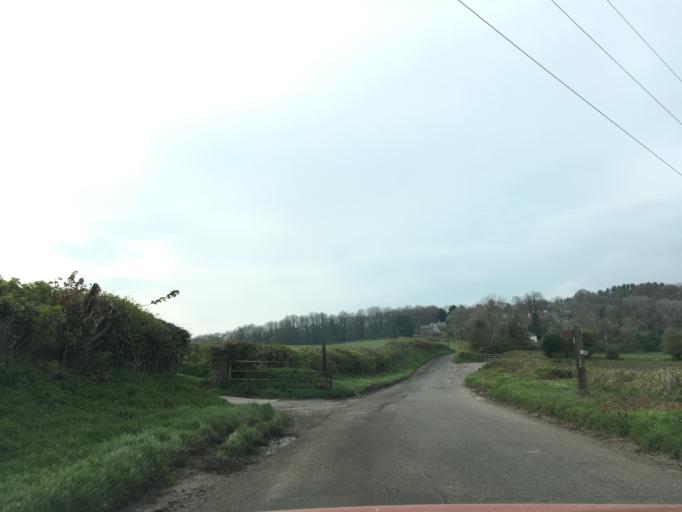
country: GB
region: Wales
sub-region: Cardiff
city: Radyr
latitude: 51.5377
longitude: -3.2324
